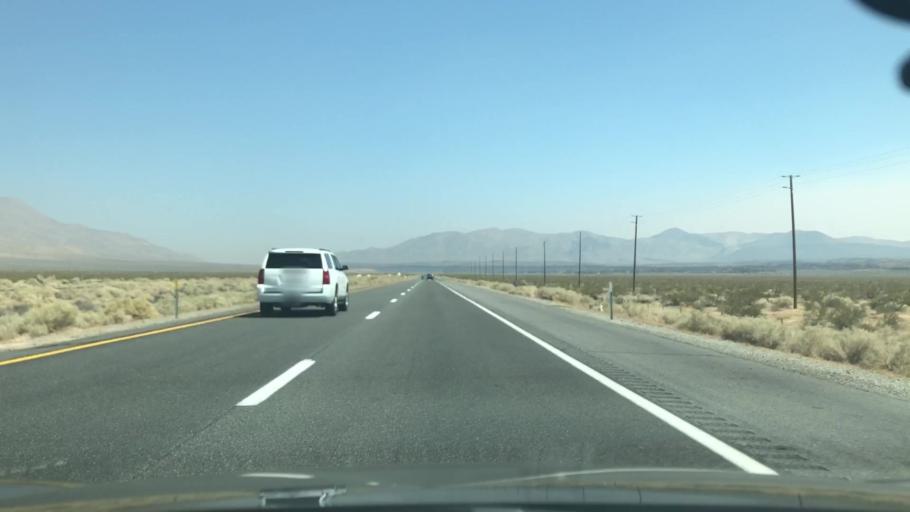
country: US
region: California
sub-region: Kern County
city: Inyokern
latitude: 35.8173
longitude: -117.8735
